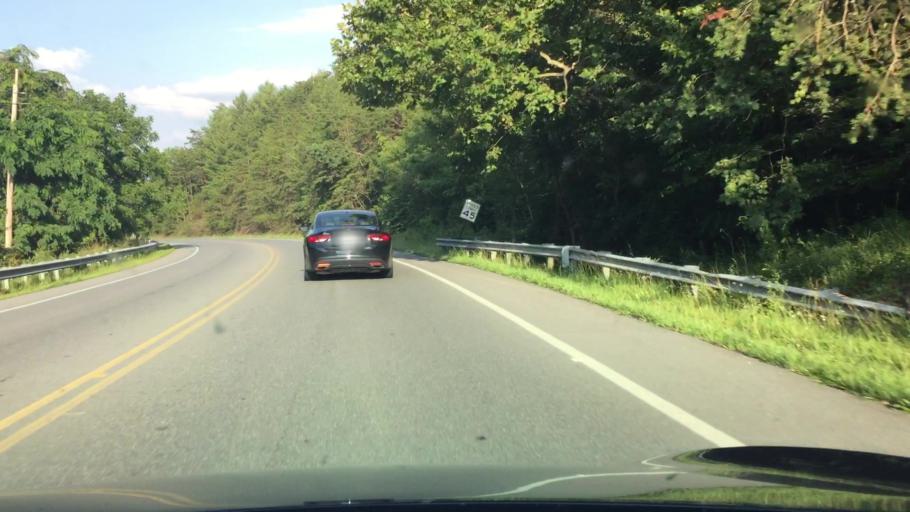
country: US
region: Virginia
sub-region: City of Radford
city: Radford
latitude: 37.1176
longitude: -80.5450
